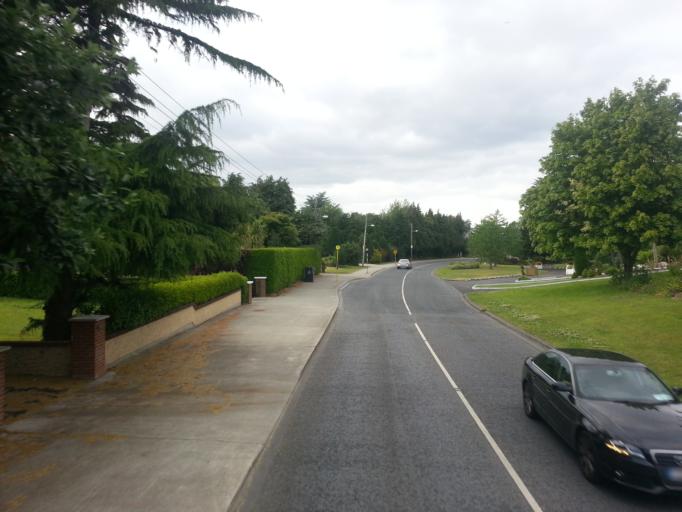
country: IE
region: Leinster
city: Sandyford
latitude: 53.2548
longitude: -6.2151
